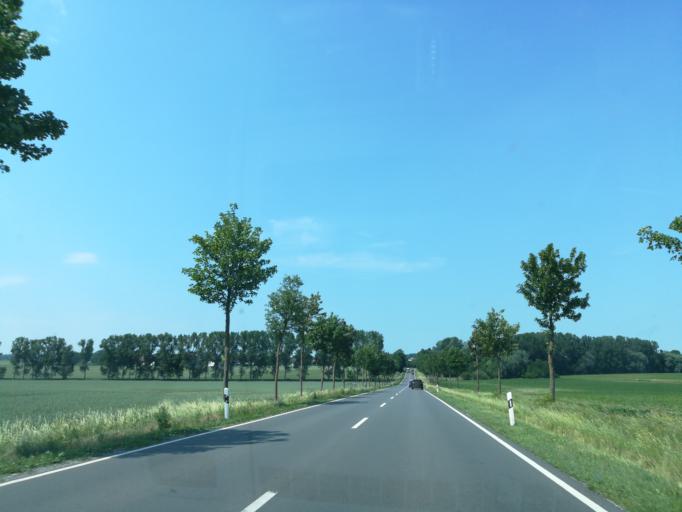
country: DE
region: Saxony-Anhalt
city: Aschersleben
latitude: 51.8122
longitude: 11.4580
